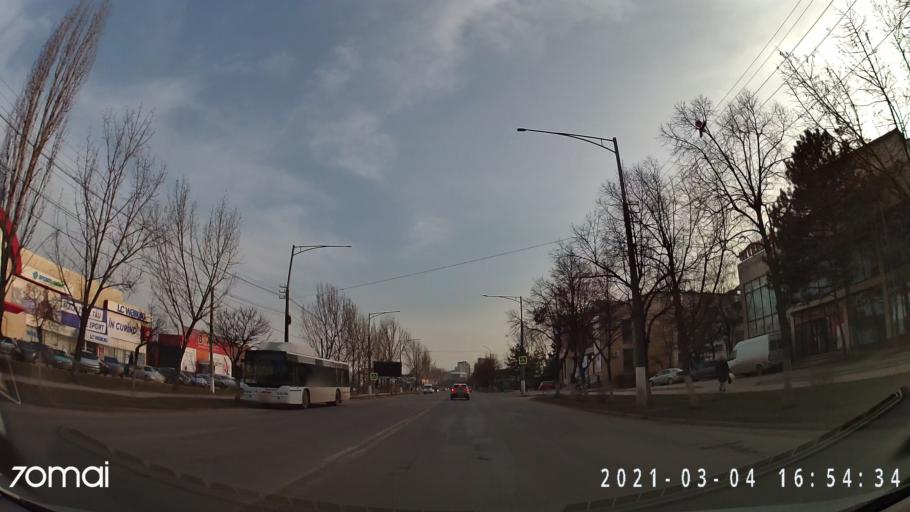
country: MD
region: Balti
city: Balti
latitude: 47.7640
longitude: 27.9413
